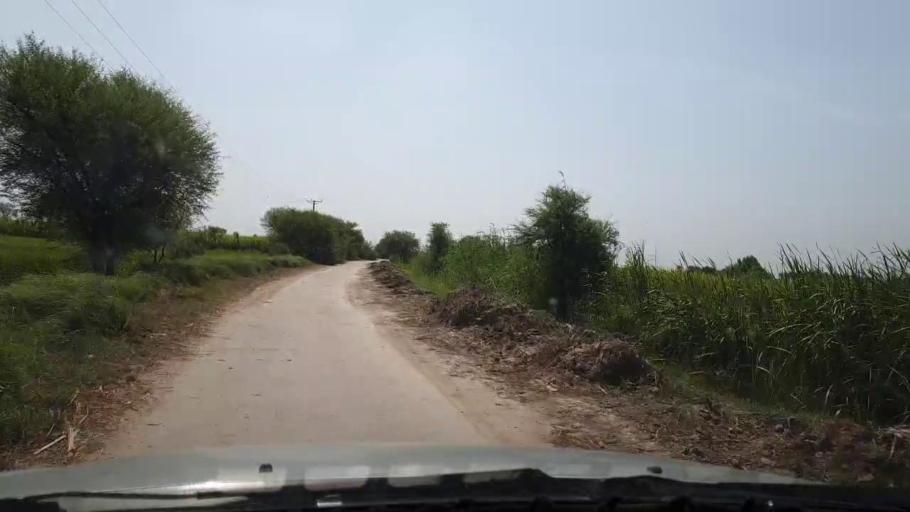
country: PK
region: Sindh
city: Tando Muhammad Khan
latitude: 25.1304
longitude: 68.6170
